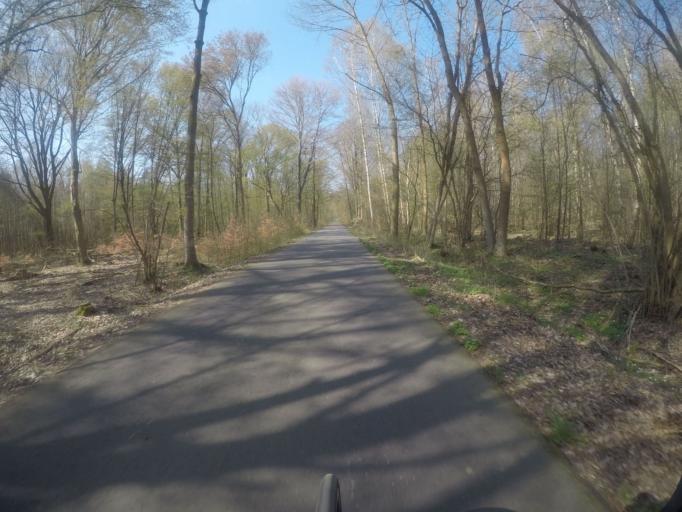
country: DE
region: Brandenburg
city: Falkensee
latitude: 52.6285
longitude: 13.1033
